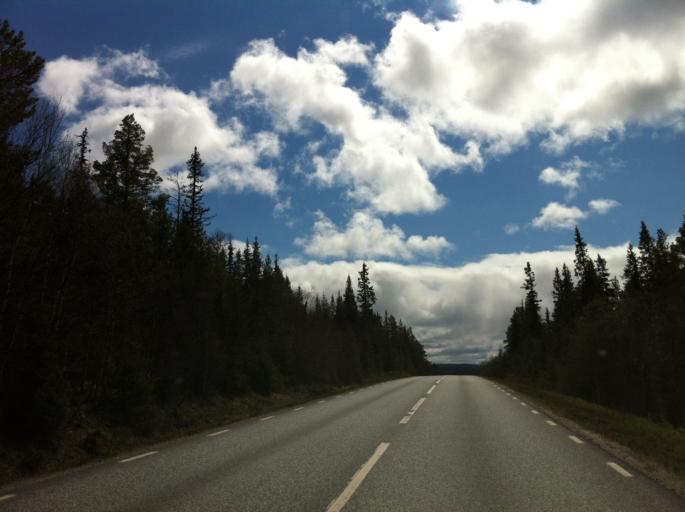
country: SE
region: Jaemtland
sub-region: Are Kommun
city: Are
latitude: 62.5813
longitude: 12.5590
